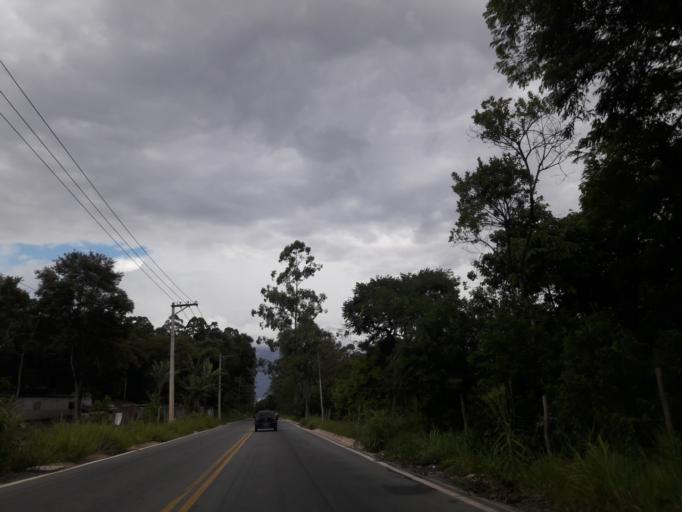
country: BR
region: Sao Paulo
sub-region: Aruja
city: Aruja
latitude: -23.3822
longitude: -46.4158
